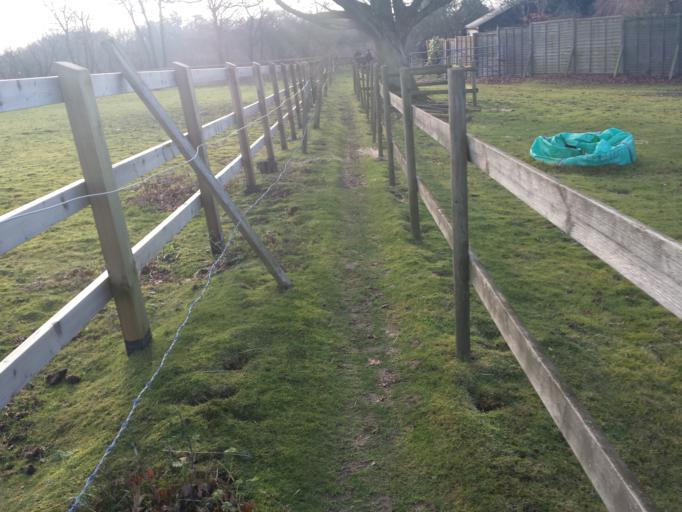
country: GB
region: England
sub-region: Essex
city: Alresford
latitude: 51.8536
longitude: 0.9828
